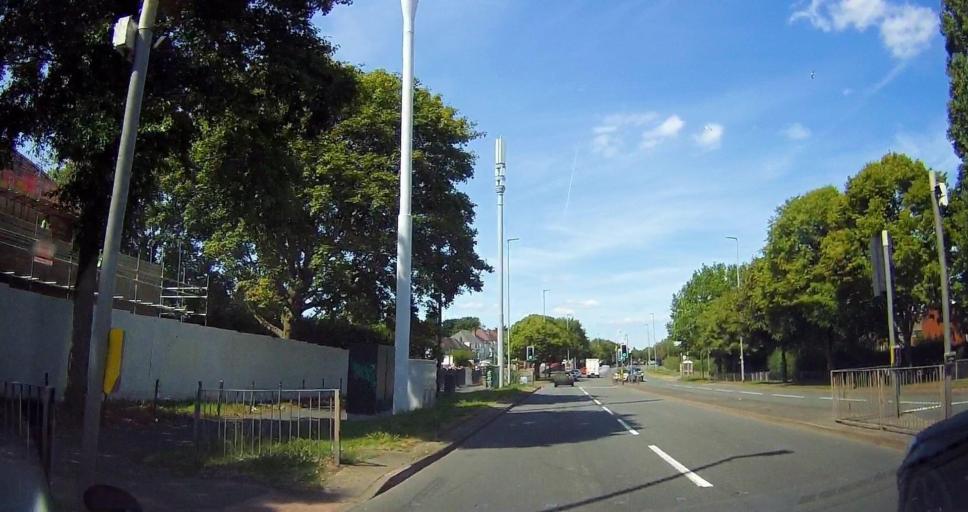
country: GB
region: England
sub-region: Wolverhampton
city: Wolverhampton
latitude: 52.5571
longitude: -2.1068
